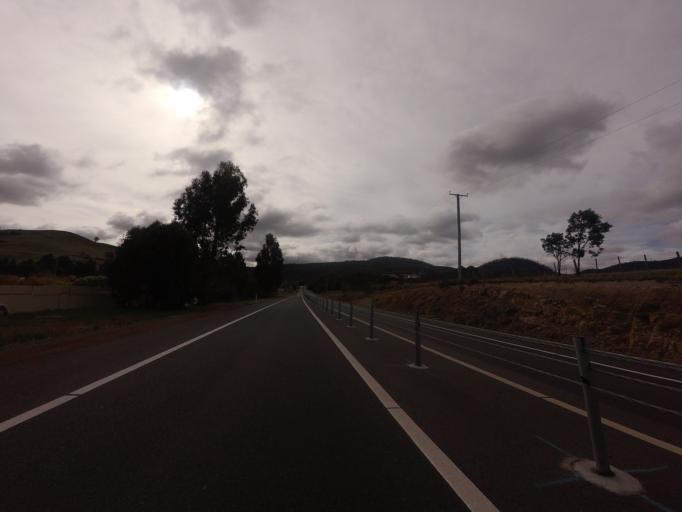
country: AU
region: Tasmania
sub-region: Brighton
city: Bridgewater
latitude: -42.5947
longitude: 147.2217
